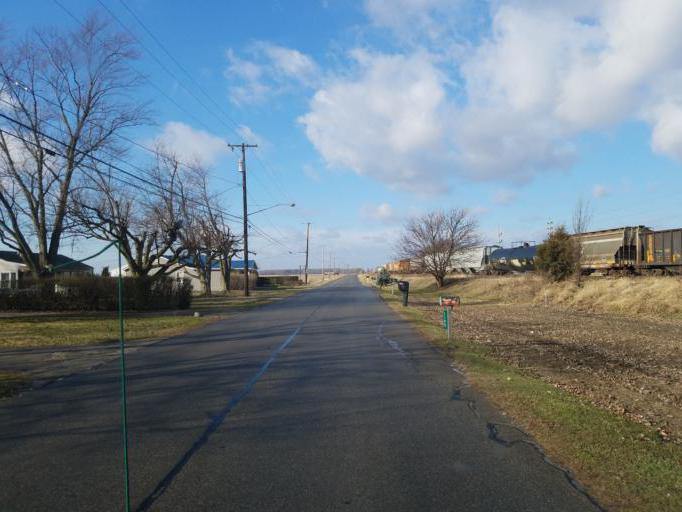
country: US
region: Ohio
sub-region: Marion County
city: Marion
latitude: 40.5858
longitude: -83.1572
